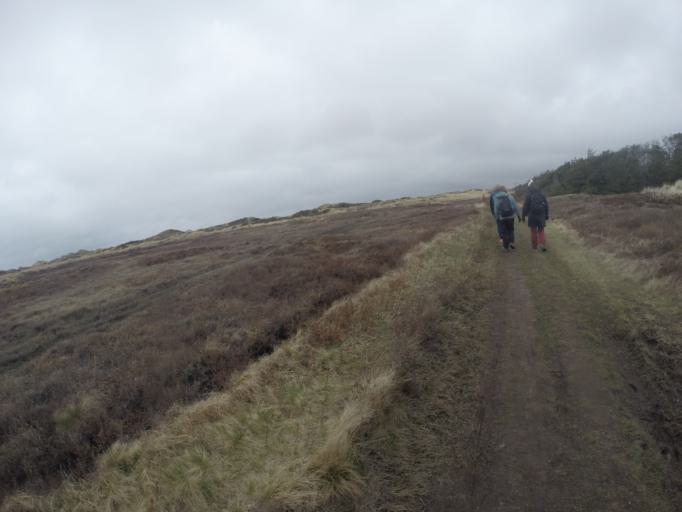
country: DK
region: North Denmark
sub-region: Thisted Kommune
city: Hurup
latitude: 56.8622
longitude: 8.2916
